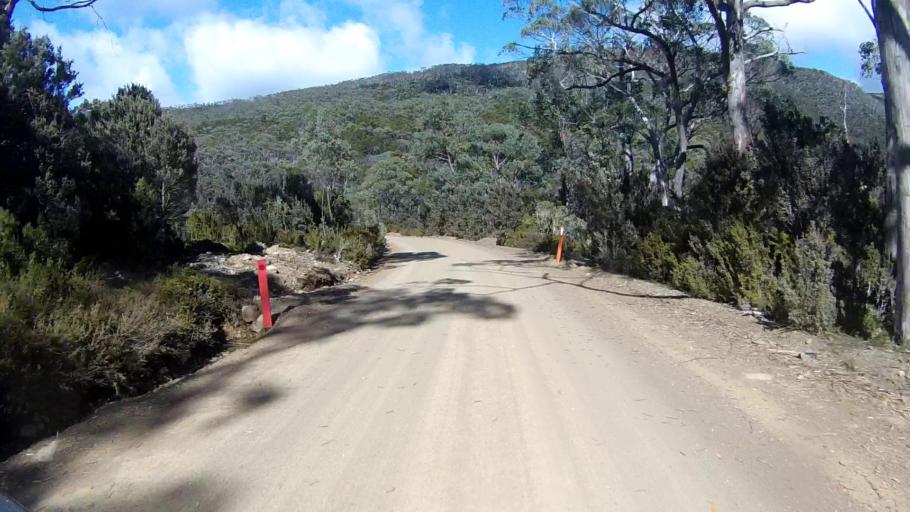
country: AU
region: Tasmania
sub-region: Derwent Valley
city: New Norfolk
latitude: -42.6875
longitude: 146.6023
